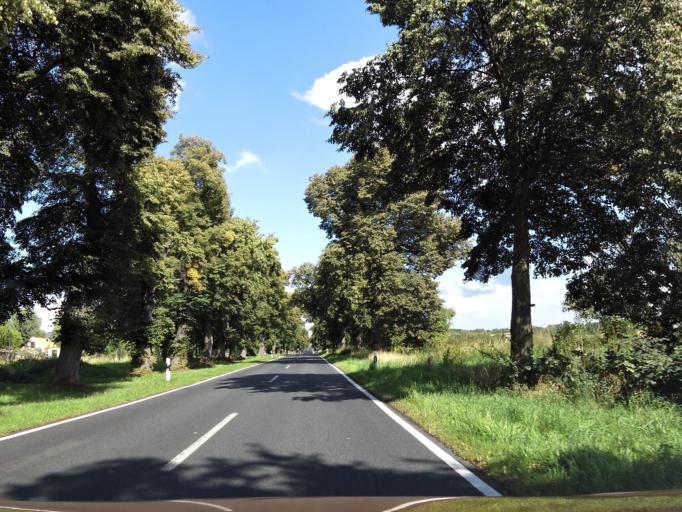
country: DE
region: Brandenburg
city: Wustermark
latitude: 52.4675
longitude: 12.9311
